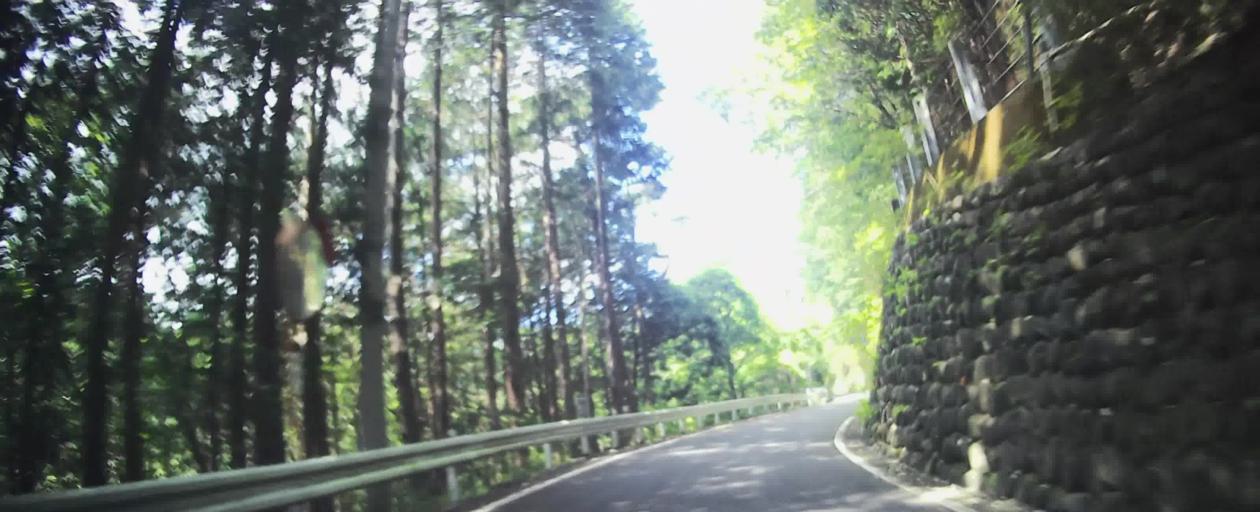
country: JP
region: Gunma
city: Kanekomachi
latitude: 36.4459
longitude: 138.9060
